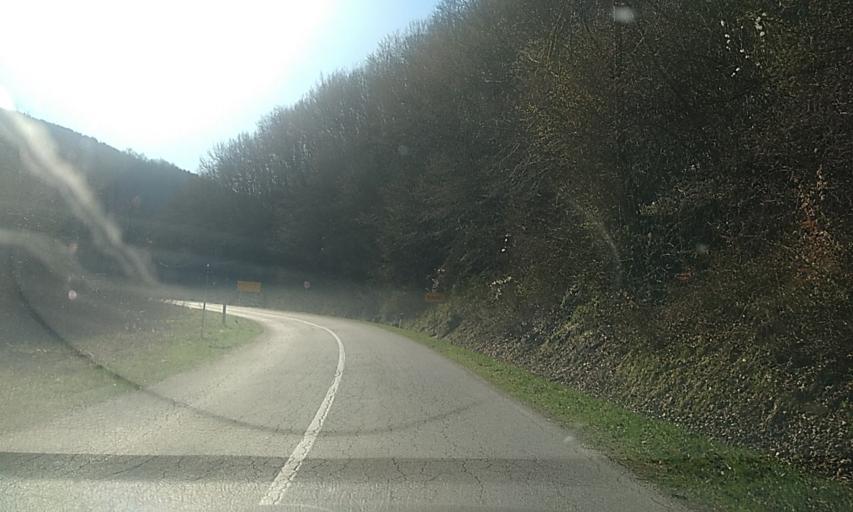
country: RS
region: Central Serbia
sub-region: Pcinjski Okrug
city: Bosilegrad
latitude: 42.4185
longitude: 22.5219
